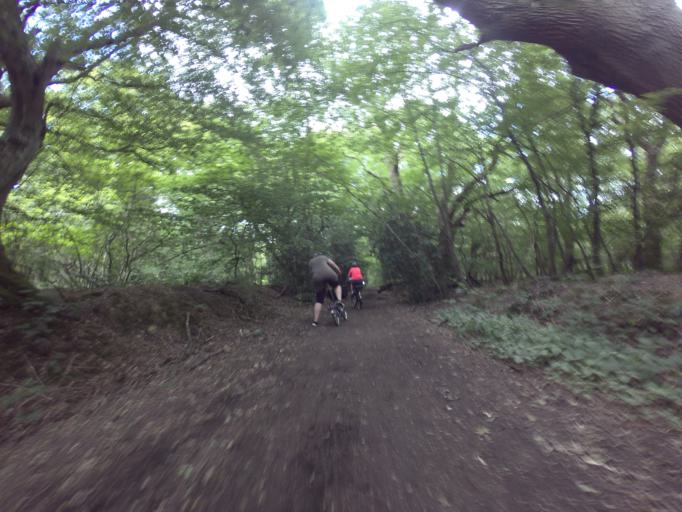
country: GB
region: England
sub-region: East Sussex
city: Hailsham
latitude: 50.8363
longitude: 0.2259
